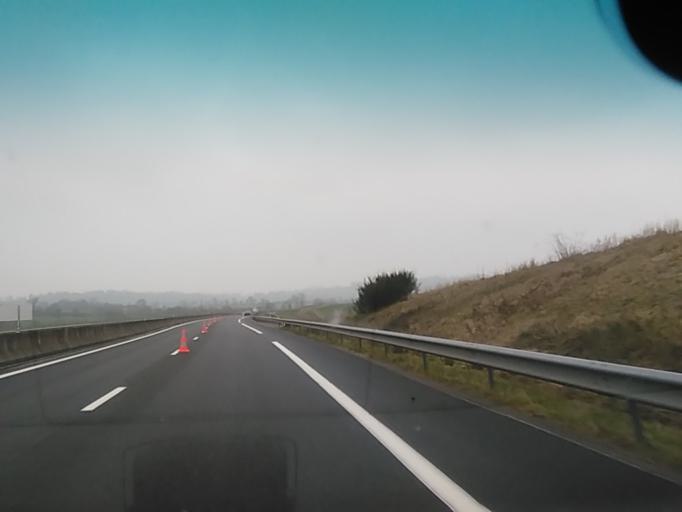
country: FR
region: Lower Normandy
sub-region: Departement de l'Orne
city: Gace
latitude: 48.7124
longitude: 0.2539
